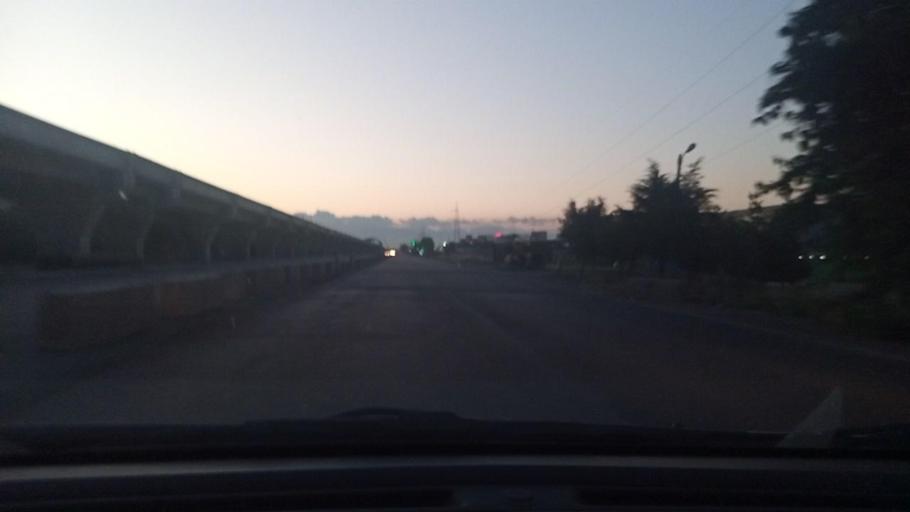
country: UZ
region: Toshkent Shahri
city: Bektemir
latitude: 41.2444
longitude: 69.2903
